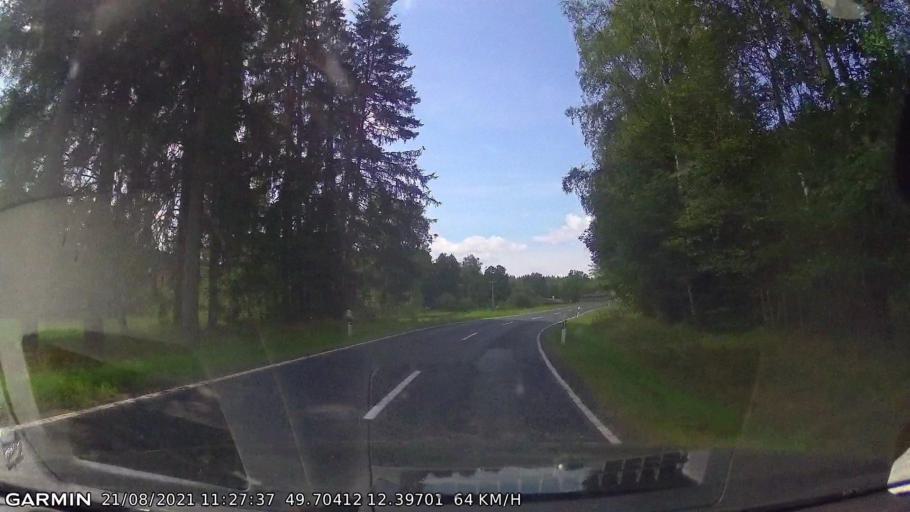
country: DE
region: Bavaria
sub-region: Upper Palatinate
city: Georgenberg
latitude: 49.7040
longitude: 12.3969
